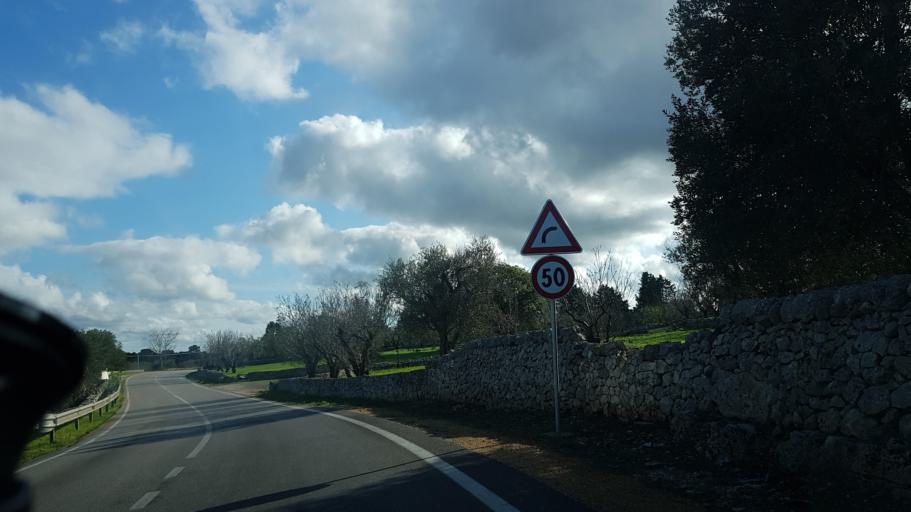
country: IT
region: Apulia
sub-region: Provincia di Brindisi
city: Ostuni
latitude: 40.6855
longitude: 17.5889
